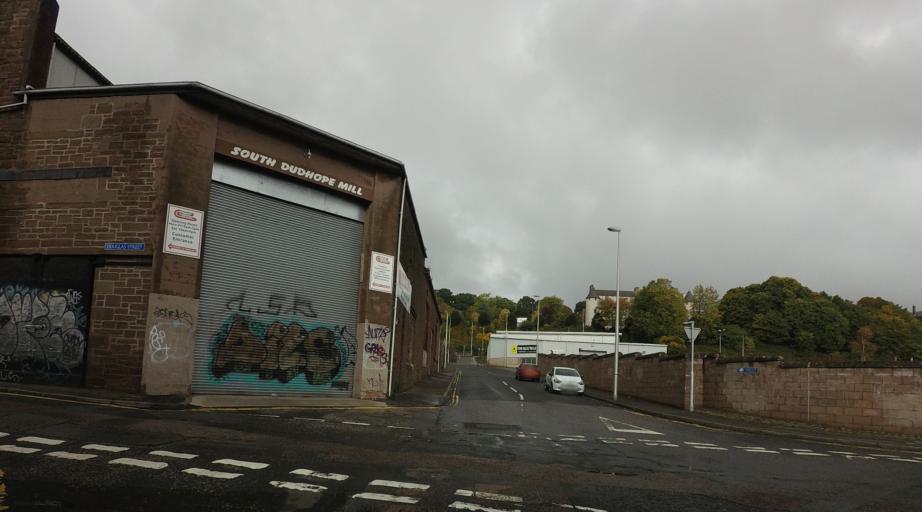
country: GB
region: Scotland
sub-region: Dundee City
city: Dundee
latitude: 56.4626
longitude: -2.9841
